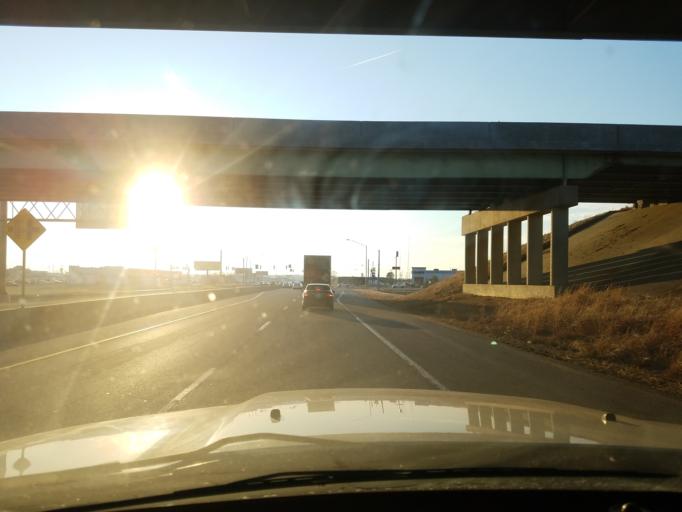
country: US
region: Indiana
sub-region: Vanderburgh County
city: Melody Hill
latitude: 37.9967
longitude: -87.4658
